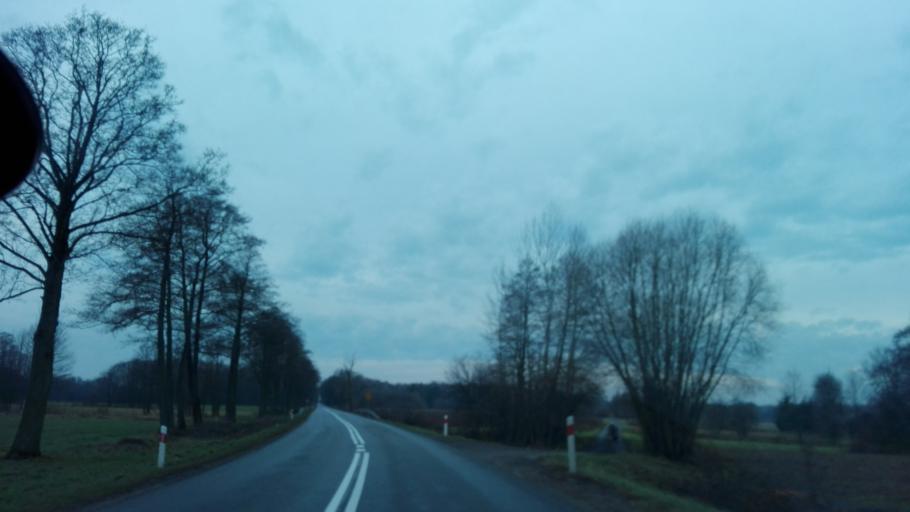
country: PL
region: Lublin Voivodeship
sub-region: Powiat radzynski
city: Wohyn
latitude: 51.7827
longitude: 22.7410
